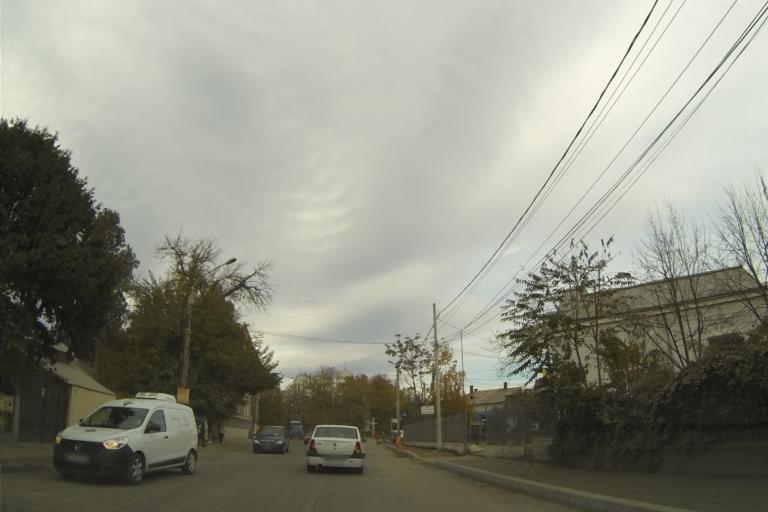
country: RO
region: Olt
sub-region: Municipiul Slatina
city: Slatina
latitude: 44.4293
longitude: 24.3542
